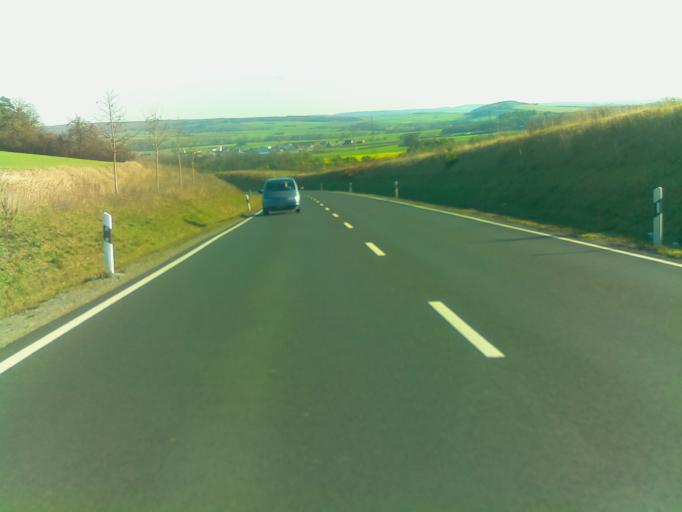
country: DE
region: Bavaria
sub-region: Regierungsbezirk Unterfranken
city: Hollstadt
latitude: 50.3298
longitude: 10.3027
